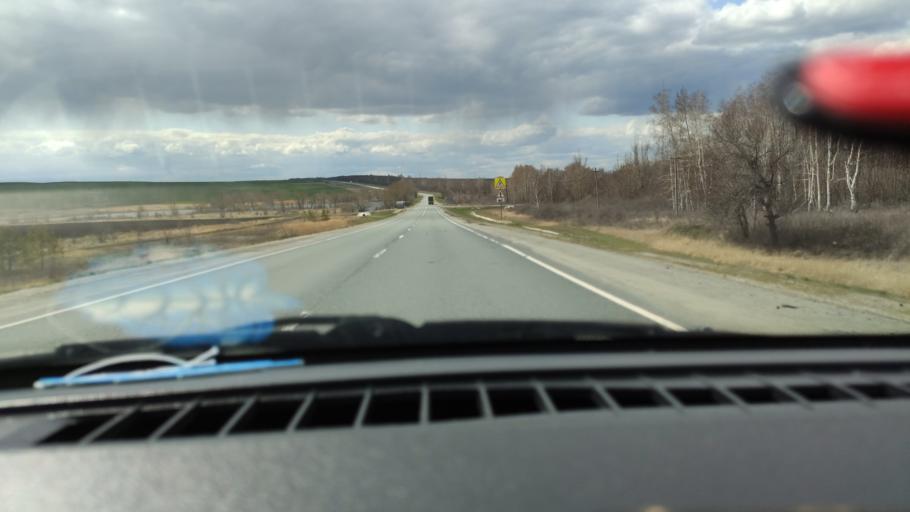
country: RU
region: Saratov
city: Alekseyevka
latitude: 52.2456
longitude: 47.9079
